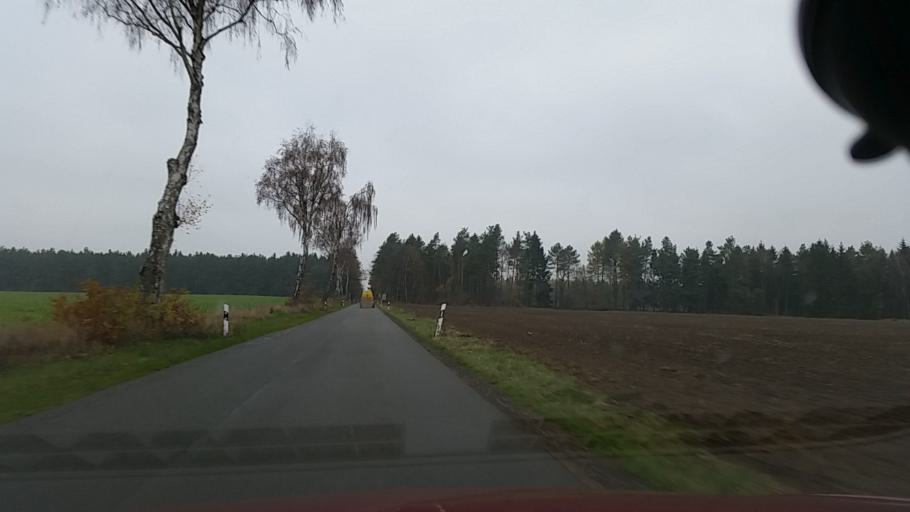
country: DE
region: Lower Saxony
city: Obernholz
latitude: 52.7782
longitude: 10.5827
